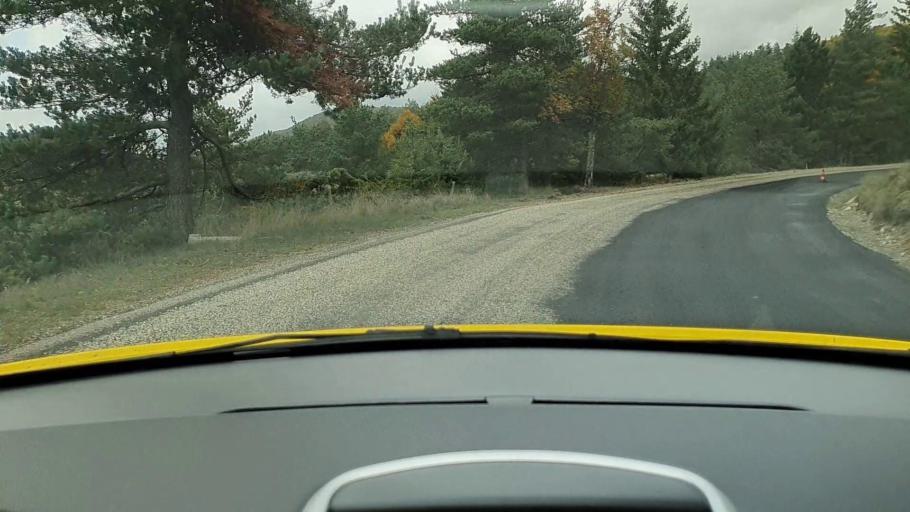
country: FR
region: Languedoc-Roussillon
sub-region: Departement du Gard
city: Valleraugue
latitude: 44.0712
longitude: 3.5369
